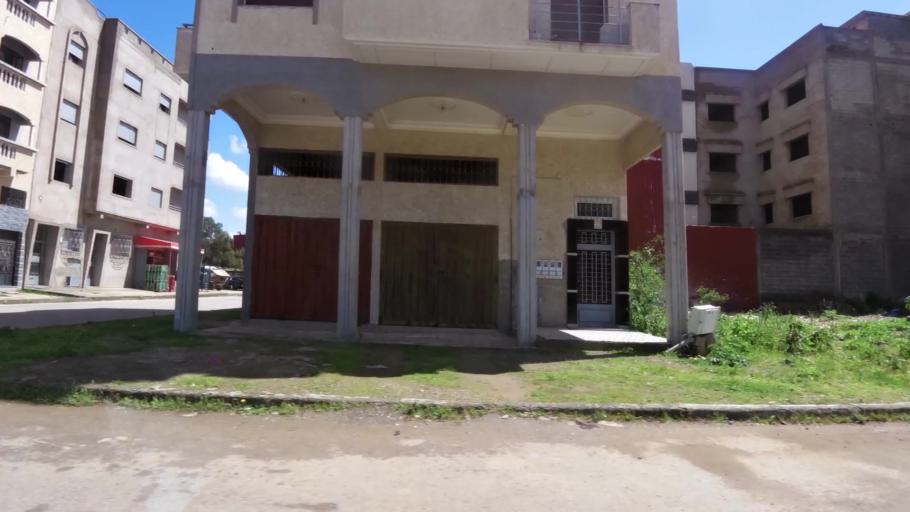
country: MA
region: Grand Casablanca
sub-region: Nouaceur
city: Dar Bouazza
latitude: 33.4154
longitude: -7.8557
